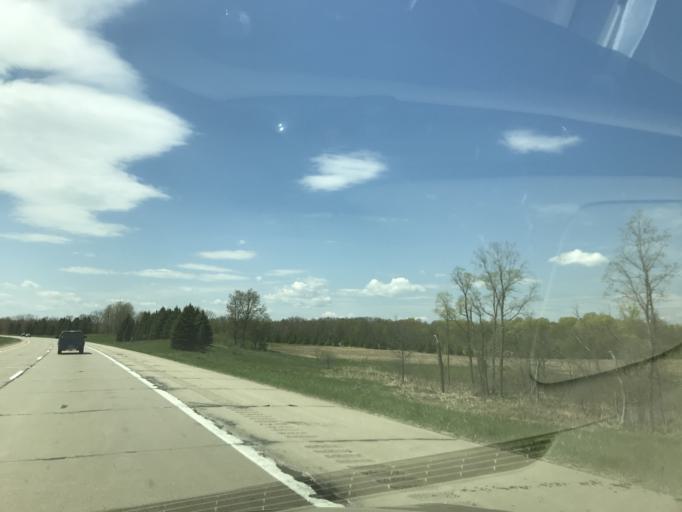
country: US
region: Michigan
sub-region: Eaton County
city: Charlotte
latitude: 42.5024
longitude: -84.8582
